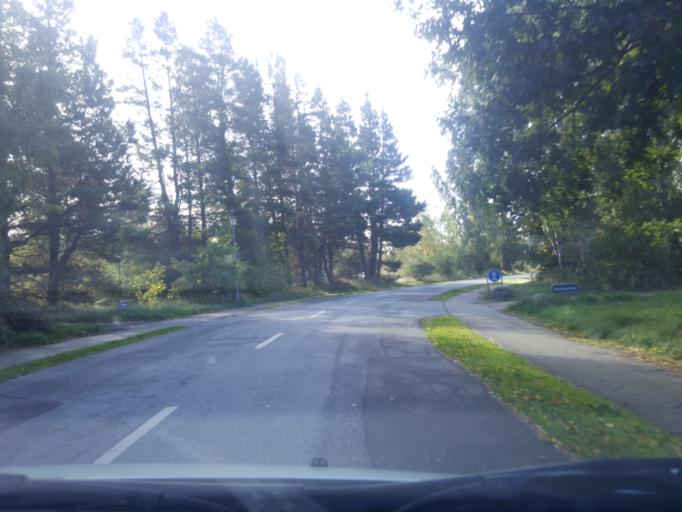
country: DK
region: Zealand
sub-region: Guldborgsund Kommune
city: Nykobing Falster
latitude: 54.6717
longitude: 11.9559
